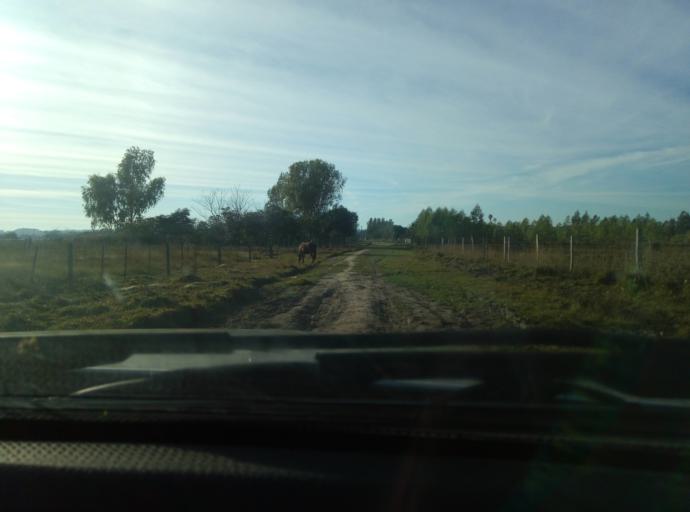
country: PY
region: Caaguazu
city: Carayao
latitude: -25.1919
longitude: -56.4095
